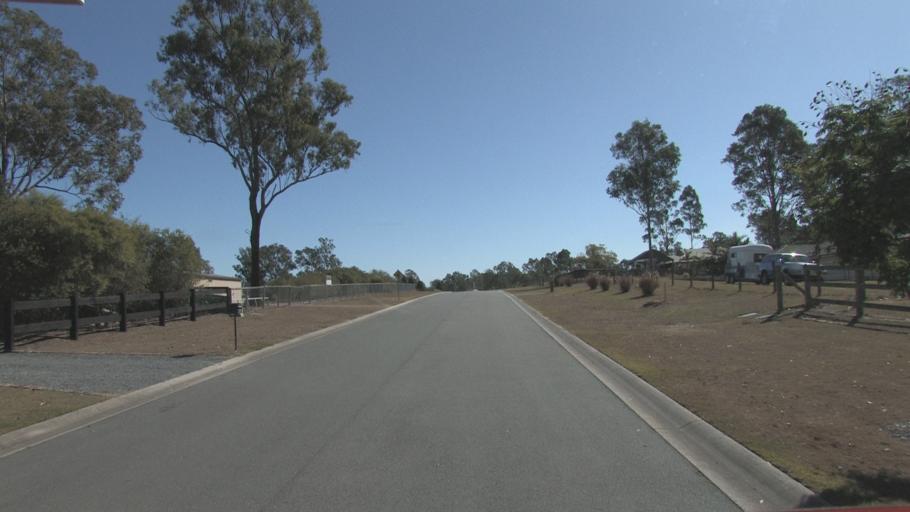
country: AU
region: Queensland
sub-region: Logan
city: Cedar Vale
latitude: -27.8603
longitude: 153.0463
